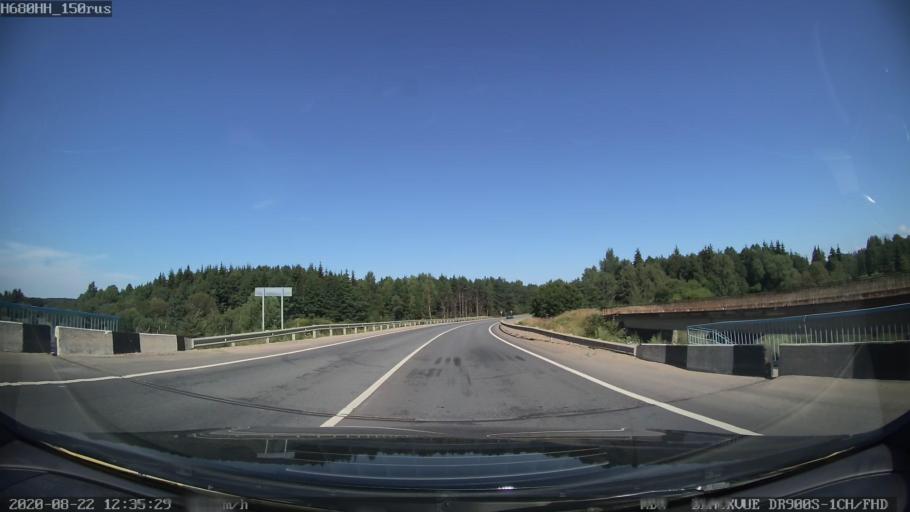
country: RU
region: Tverskaya
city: Rameshki
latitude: 57.2727
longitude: 36.0715
